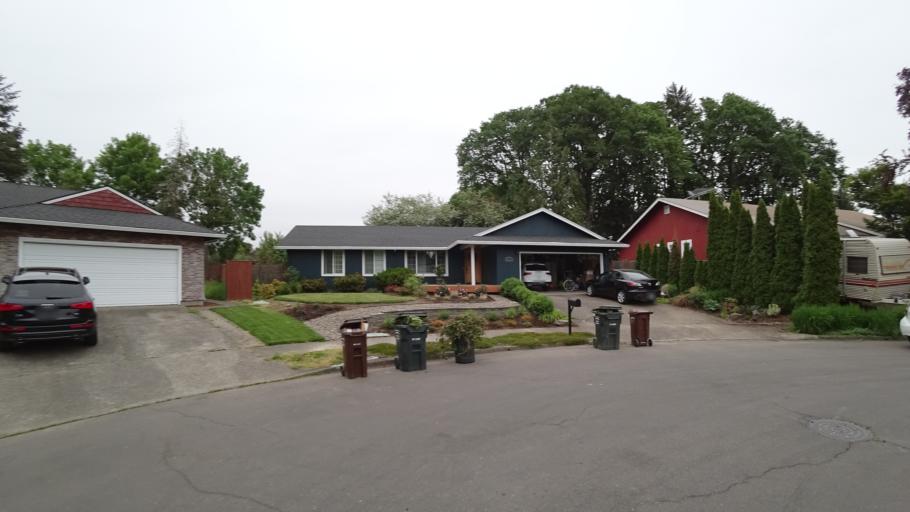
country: US
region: Oregon
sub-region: Washington County
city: Bethany
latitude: 45.5419
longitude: -122.8598
